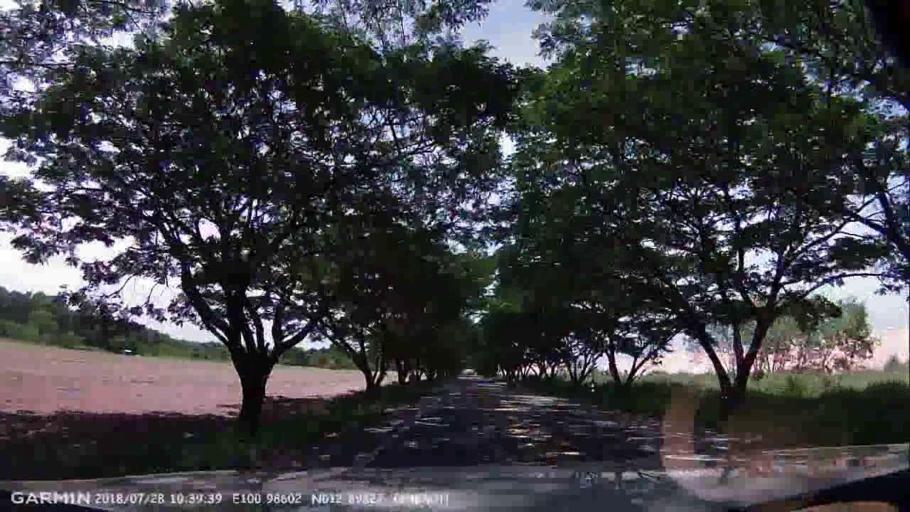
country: TH
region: Chon Buri
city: Phatthaya
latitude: 12.8982
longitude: 100.9860
